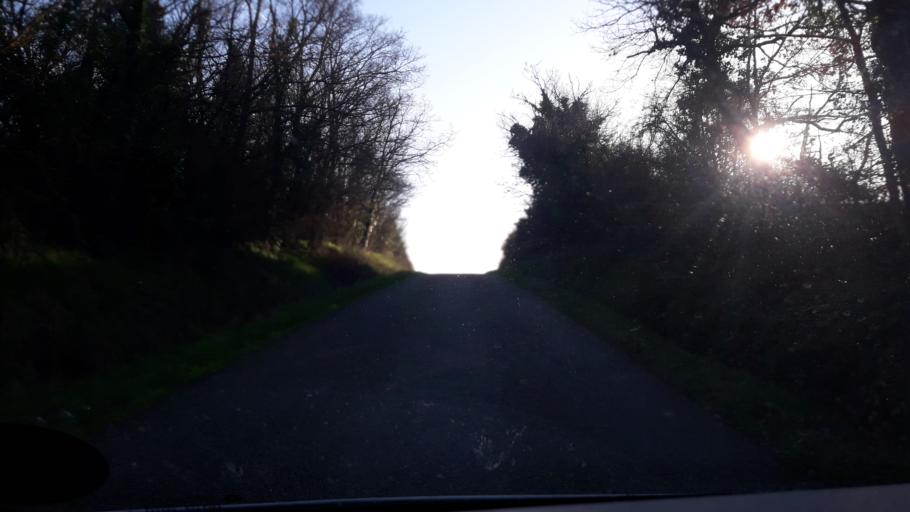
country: FR
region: Midi-Pyrenees
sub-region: Departement du Gers
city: Gimont
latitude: 43.6386
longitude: 0.9843
